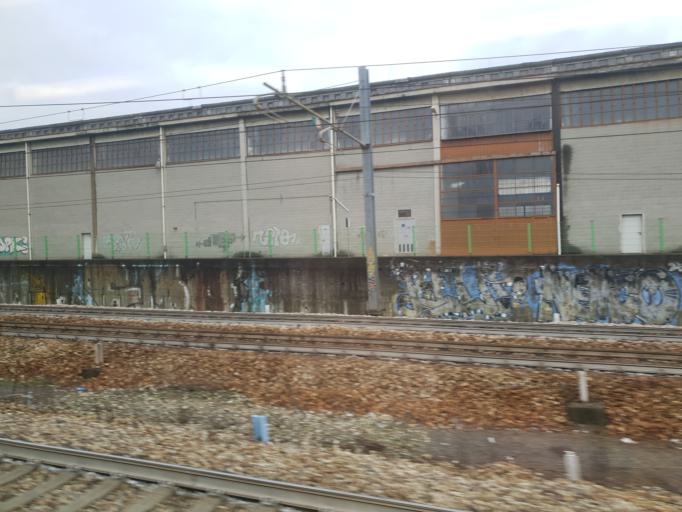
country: IT
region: Lombardy
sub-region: Citta metropolitana di Milano
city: Novate Milanese
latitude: 45.5071
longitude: 9.1559
